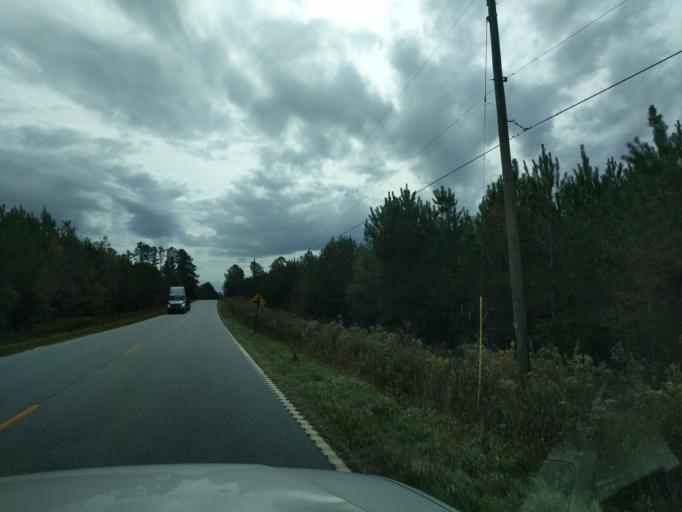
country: US
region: South Carolina
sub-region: Saluda County
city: Saluda
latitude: 34.0764
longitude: -81.8204
